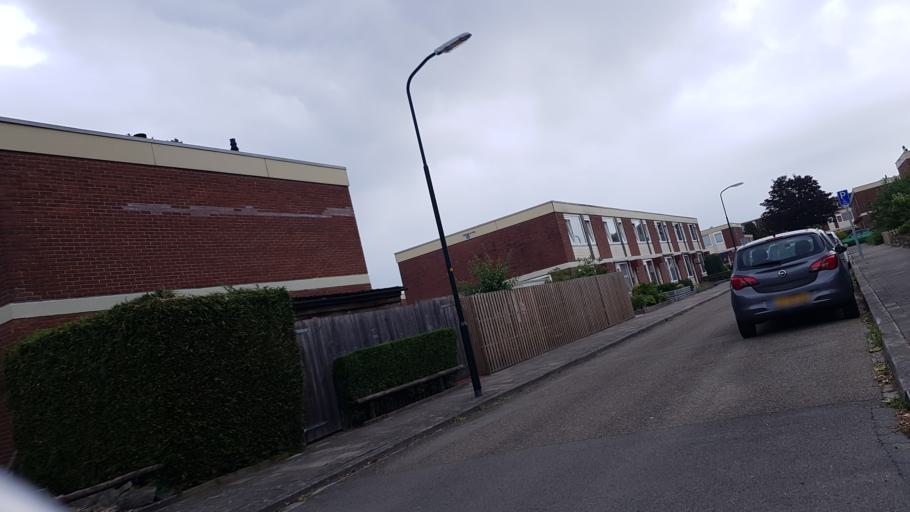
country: NL
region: Gelderland
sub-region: Gemeente Apeldoorn
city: Apeldoorn
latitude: 52.1891
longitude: 5.9753
